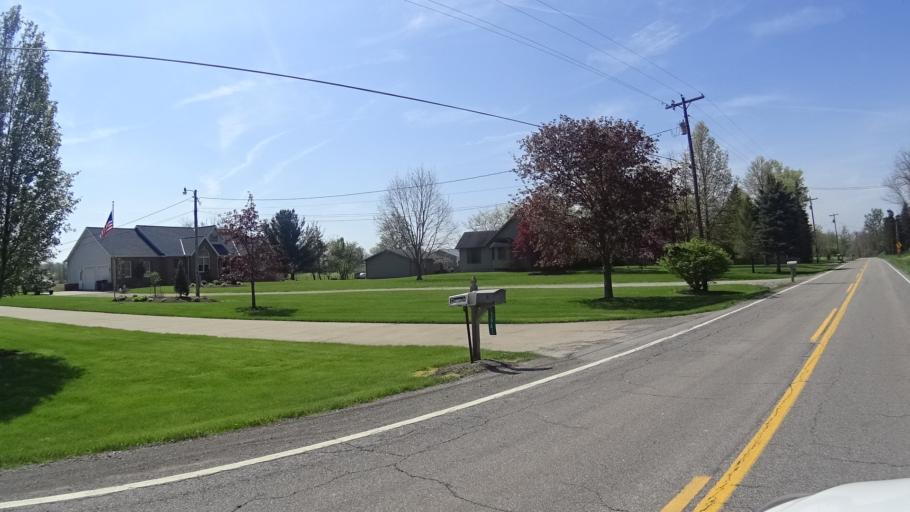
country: US
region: Ohio
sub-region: Lorain County
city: Lagrange
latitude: 41.2852
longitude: -82.1472
